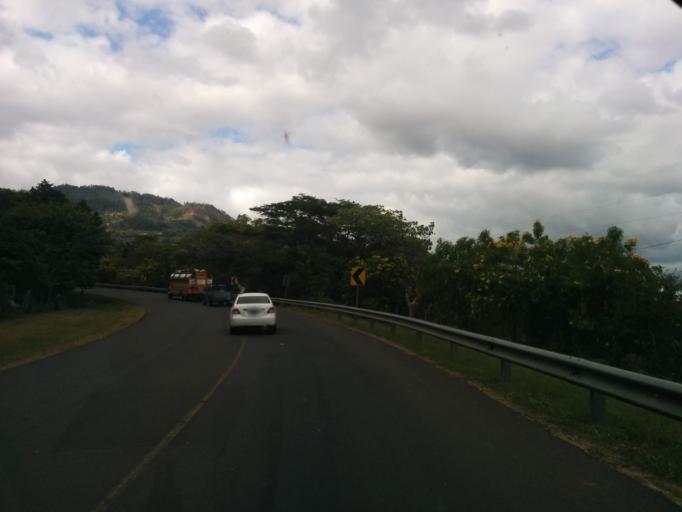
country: NI
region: Esteli
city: Esteli
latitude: 12.9979
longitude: -86.2841
